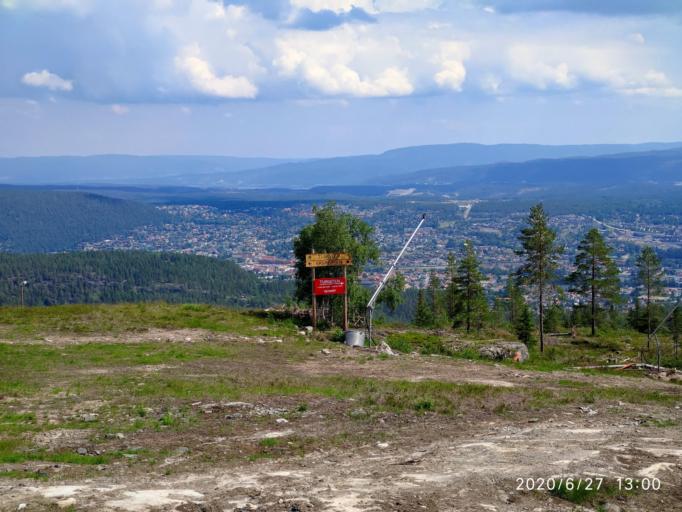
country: NO
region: Buskerud
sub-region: Kongsberg
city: Kongsberg
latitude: 59.6573
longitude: 9.5981
